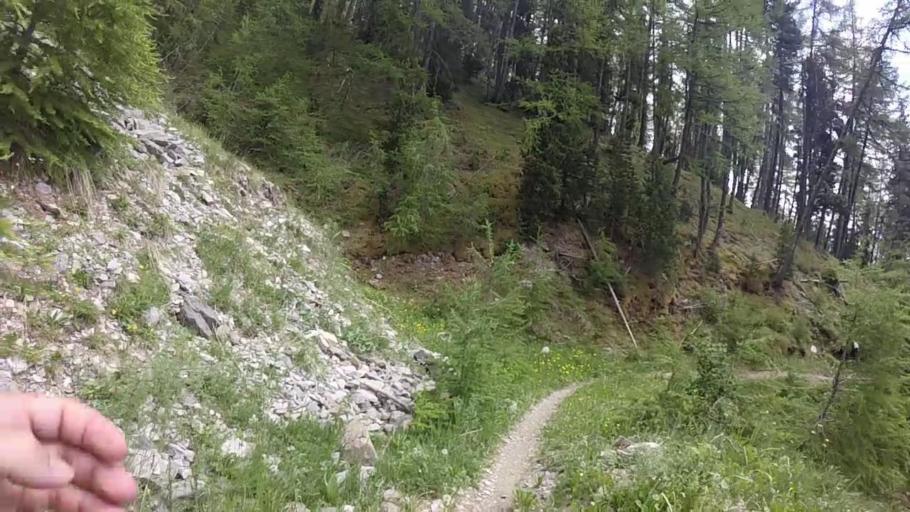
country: FR
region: Provence-Alpes-Cote d'Azur
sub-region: Departement des Alpes-de-Haute-Provence
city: Seyne-les-Alpes
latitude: 44.4099
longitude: 6.3724
